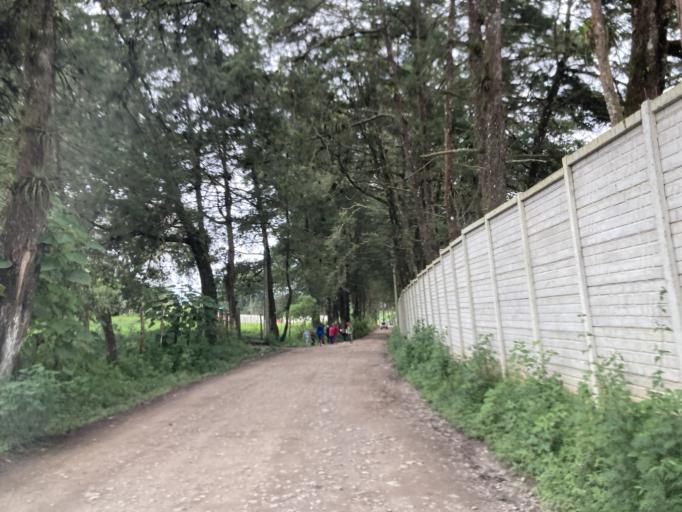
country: GT
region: Guatemala
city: San Jose Pinula
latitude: 14.5325
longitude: -90.4057
